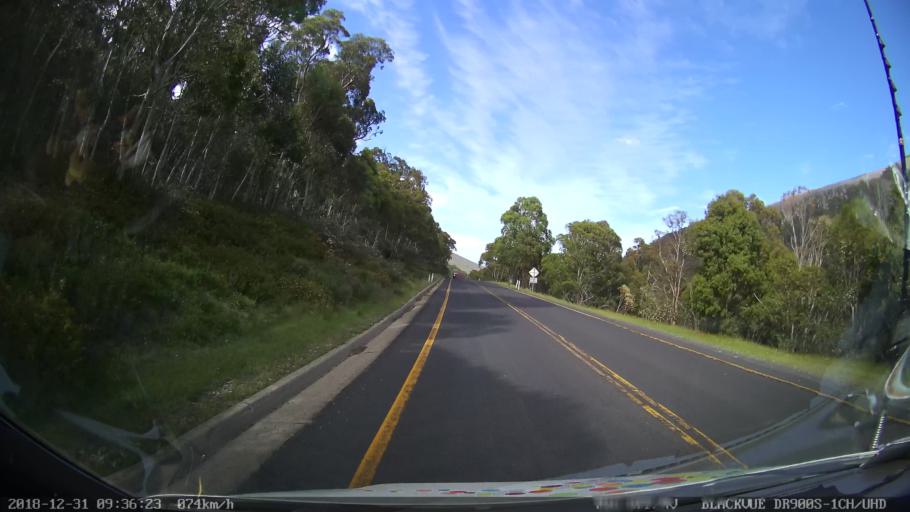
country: AU
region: New South Wales
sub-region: Snowy River
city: Jindabyne
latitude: -36.4583
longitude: 148.3871
